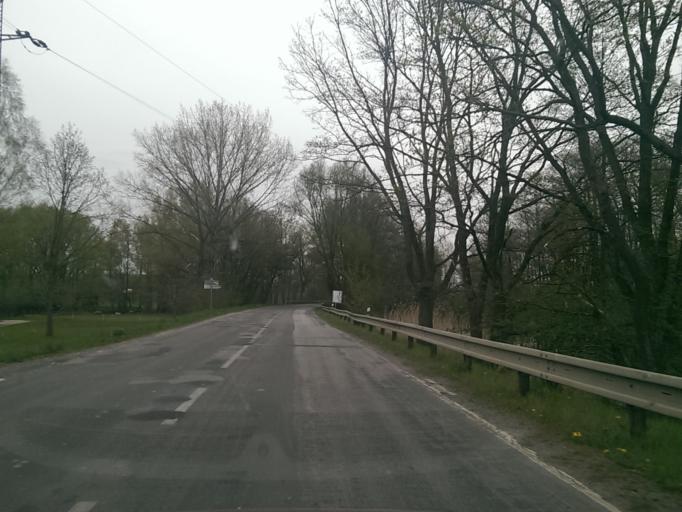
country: CZ
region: Central Bohemia
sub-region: Okres Mlada Boleslav
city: Zd'ar
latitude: 50.5488
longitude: 15.0464
